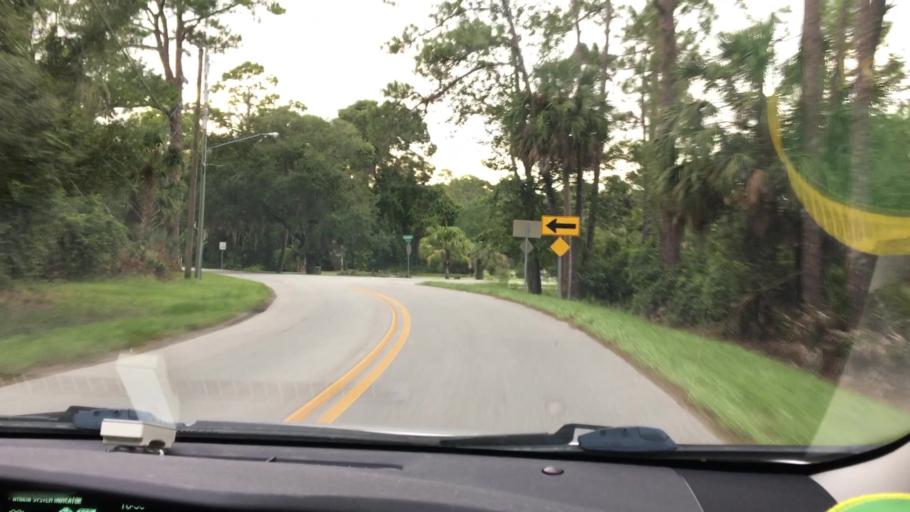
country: US
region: Florida
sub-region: Volusia County
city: Deltona
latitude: 28.8598
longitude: -81.2313
